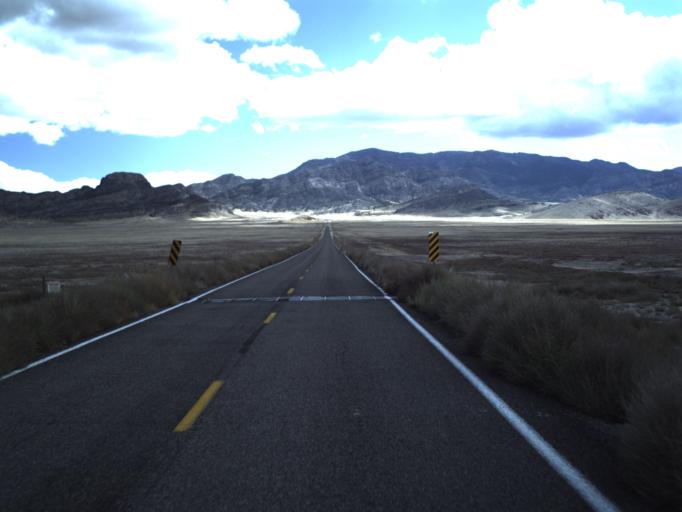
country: US
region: Utah
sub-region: Beaver County
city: Milford
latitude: 38.5206
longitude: -113.6503
